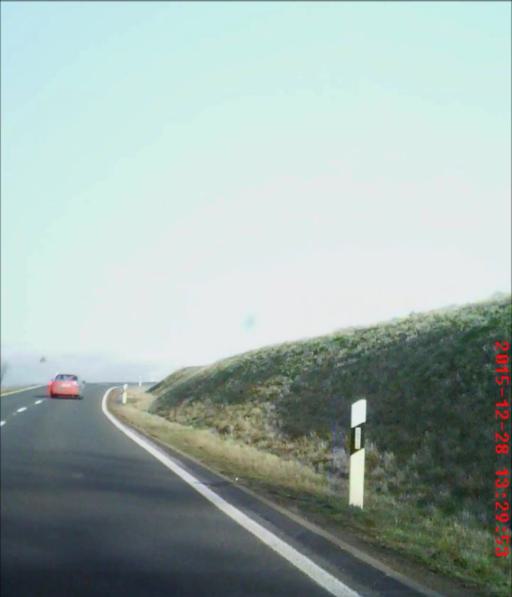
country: DE
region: Thuringia
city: Eberstedt
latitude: 51.0727
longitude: 11.5907
